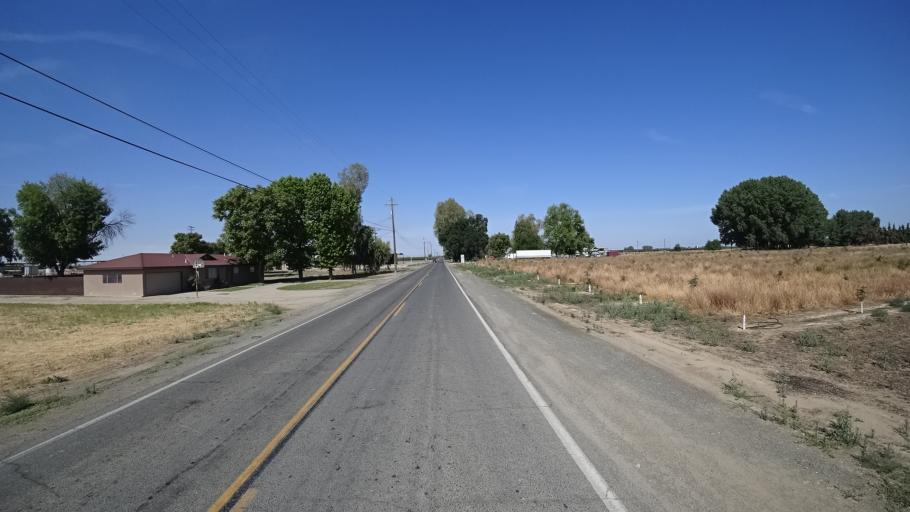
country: US
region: California
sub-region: Kings County
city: Armona
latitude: 36.2548
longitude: -119.7093
